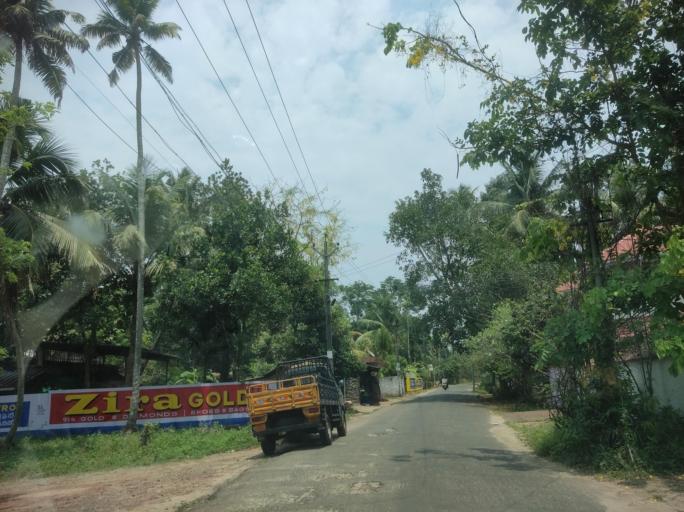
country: IN
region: Kerala
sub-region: Alappuzha
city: Vayalar
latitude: 9.7484
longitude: 76.3247
